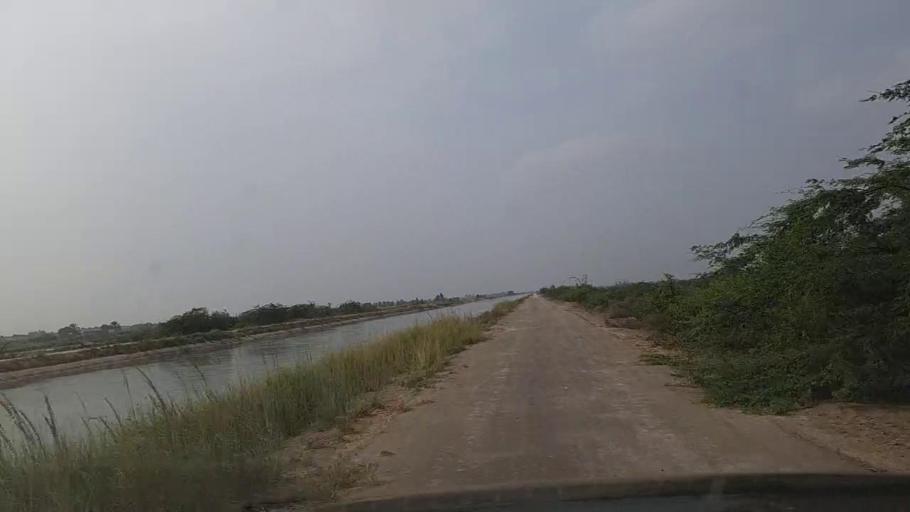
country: PK
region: Sindh
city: Thatta
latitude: 24.8040
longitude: 67.8961
